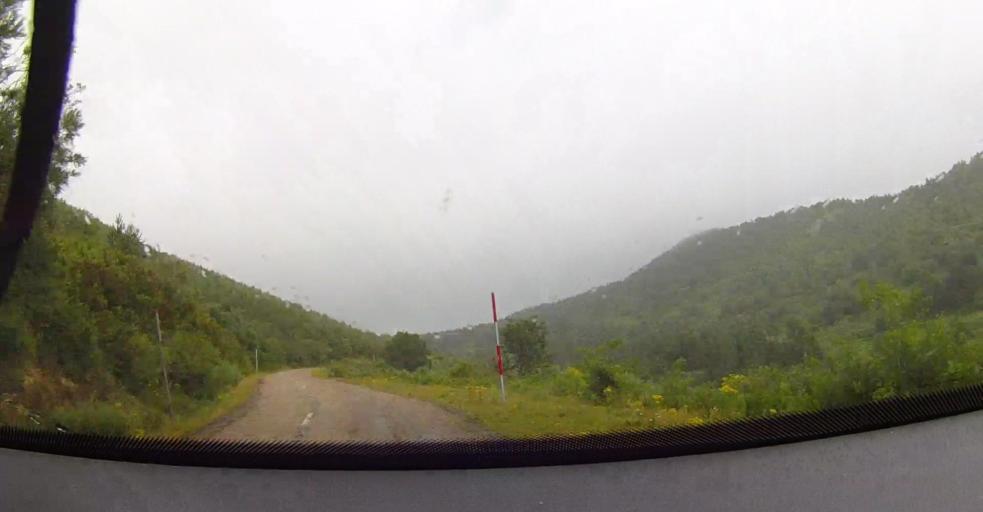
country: ES
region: Castille and Leon
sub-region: Provincia de Leon
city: Puebla de Lillo
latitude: 43.0748
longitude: -5.2537
